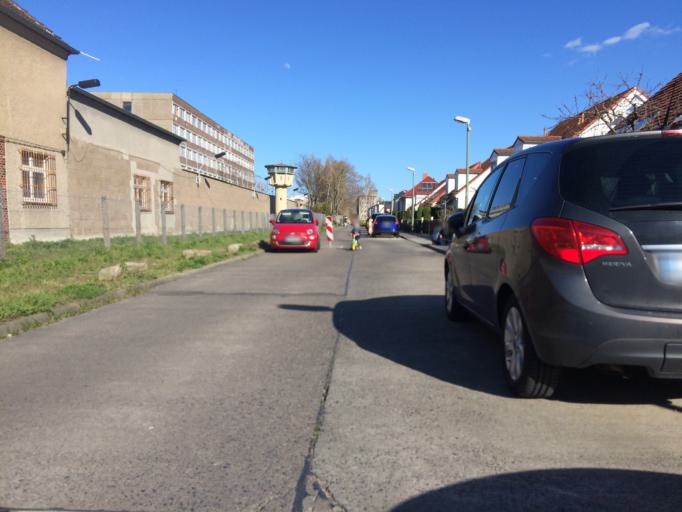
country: DE
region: Berlin
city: Alt-Hohenschoenhausen
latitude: 52.5412
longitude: 13.5013
